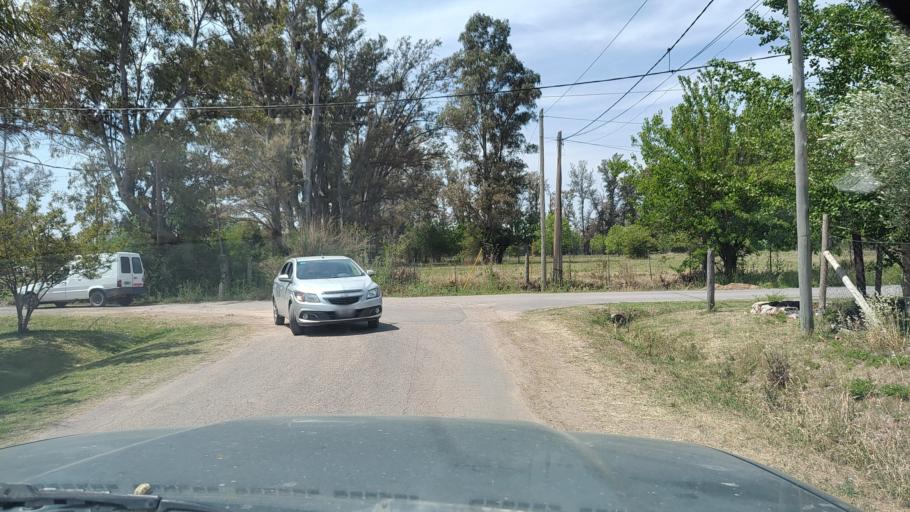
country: AR
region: Buenos Aires
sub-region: Partido de Lujan
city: Lujan
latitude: -34.6008
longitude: -59.1702
